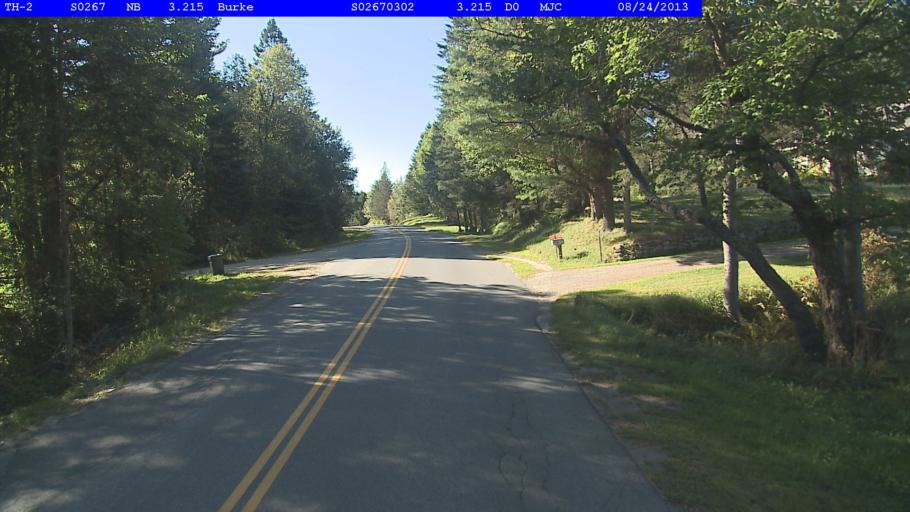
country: US
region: Vermont
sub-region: Caledonia County
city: Lyndonville
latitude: 44.6241
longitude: -71.9577
